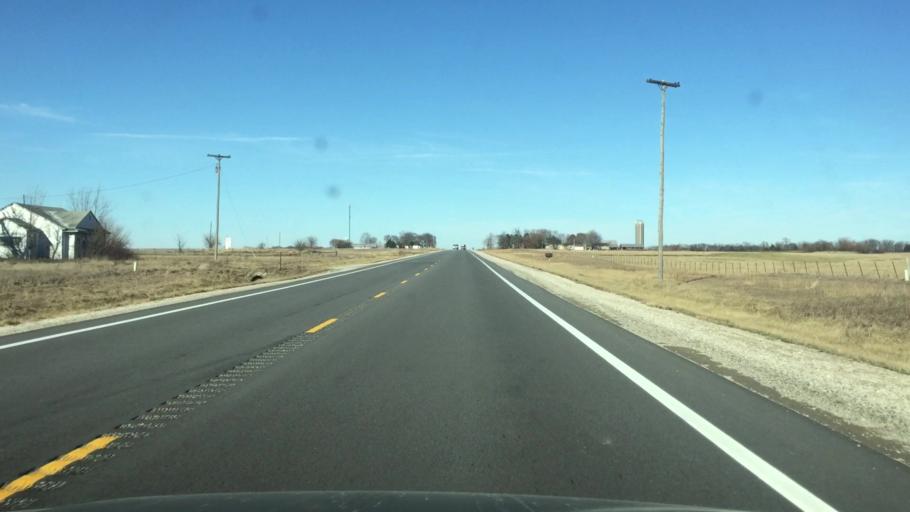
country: US
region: Kansas
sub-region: Anderson County
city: Garnett
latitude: 38.3781
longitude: -95.2488
